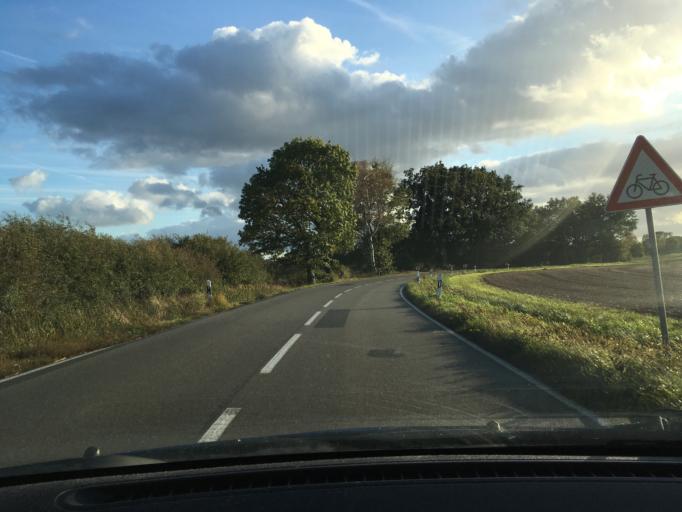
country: DE
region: Lower Saxony
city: Hittbergen
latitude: 53.3323
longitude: 10.5991
